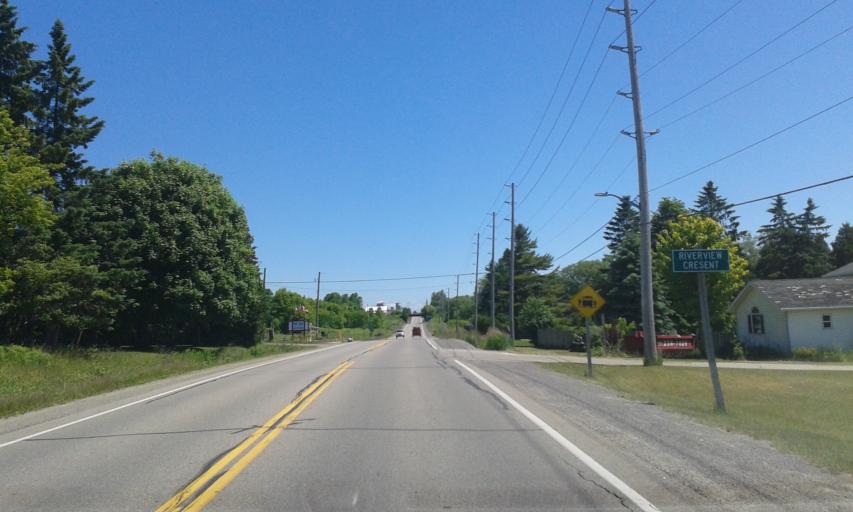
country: CA
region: Ontario
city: Prescott
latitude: 44.7178
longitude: -75.4988
